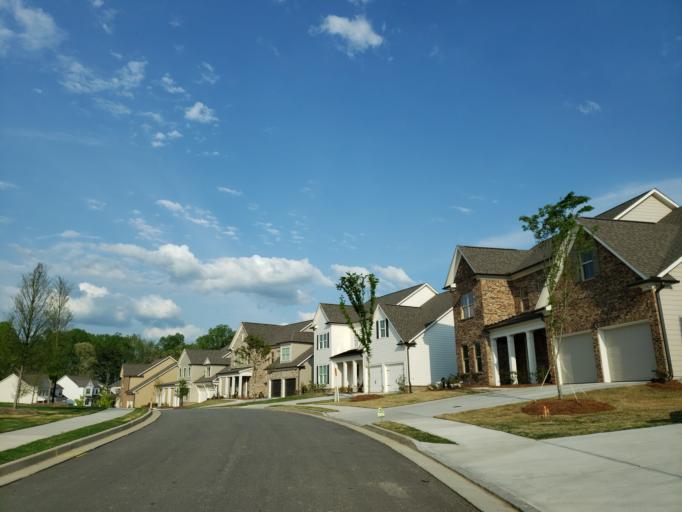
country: US
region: Georgia
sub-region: Cherokee County
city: Holly Springs
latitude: 34.1684
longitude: -84.4339
